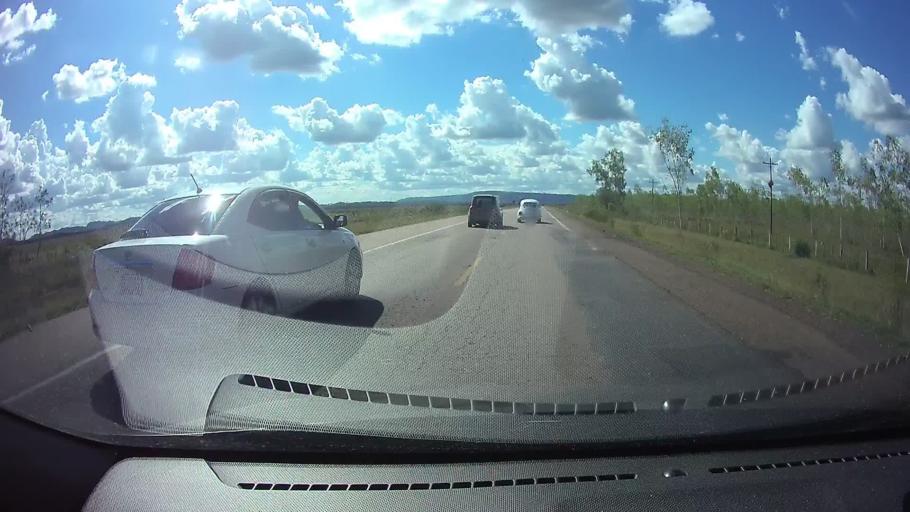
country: PY
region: Paraguari
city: Sapucai
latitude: -25.7427
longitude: -56.8085
